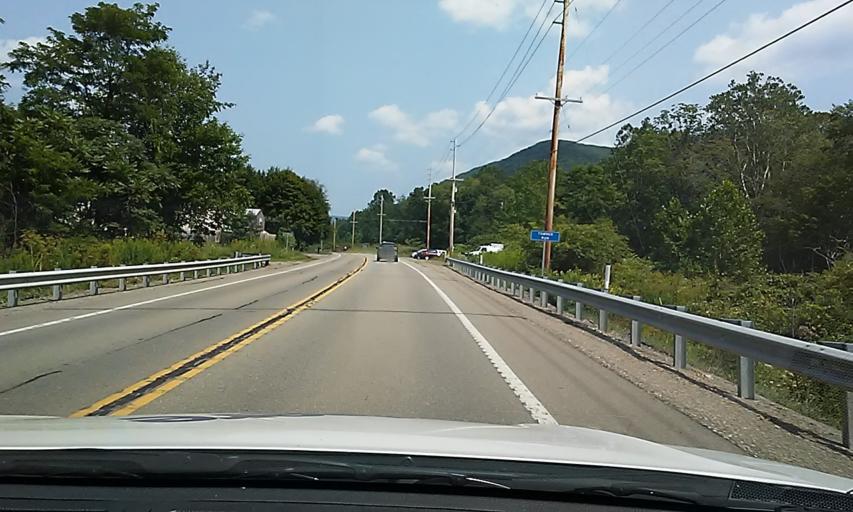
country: US
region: Pennsylvania
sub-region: Cameron County
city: Emporium
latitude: 41.4934
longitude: -78.2789
